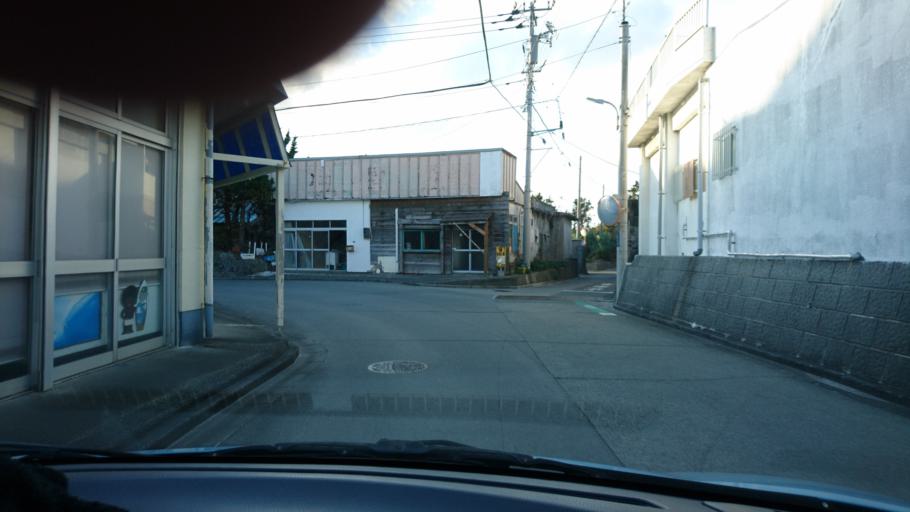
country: JP
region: Shizuoka
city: Shimoda
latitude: 34.3773
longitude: 139.2541
